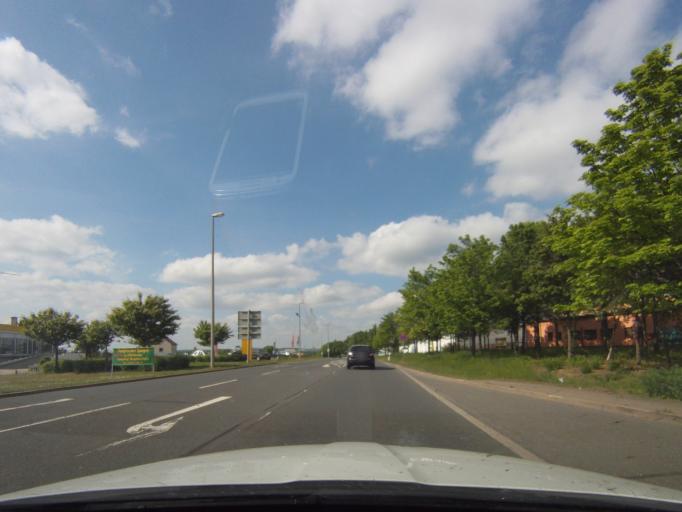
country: DE
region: Thuringia
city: Gera
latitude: 50.8760
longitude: 12.1165
